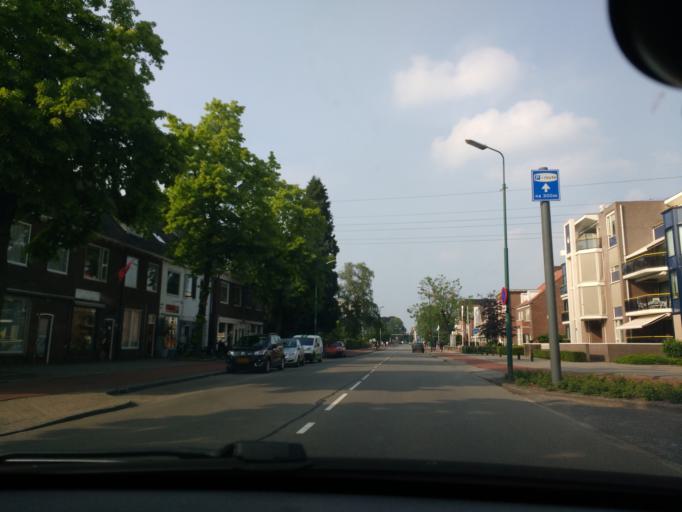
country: NL
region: Utrecht
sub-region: Gemeente Veenendaal
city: Veenendaal
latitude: 52.0209
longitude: 5.5511
